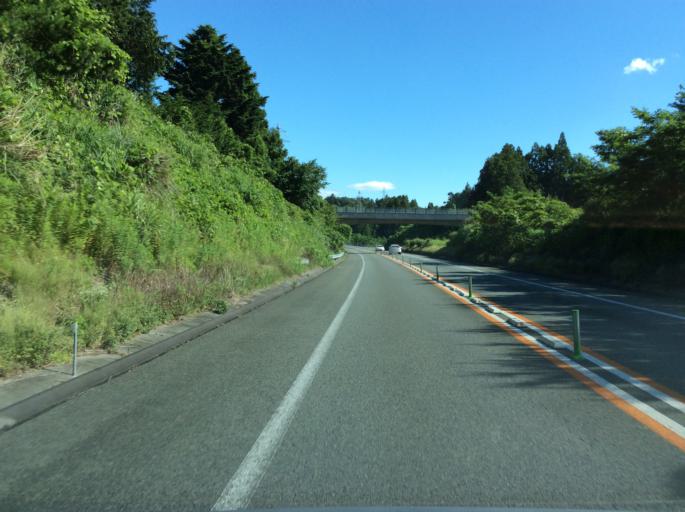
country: JP
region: Fukushima
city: Namie
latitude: 37.3375
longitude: 140.9907
